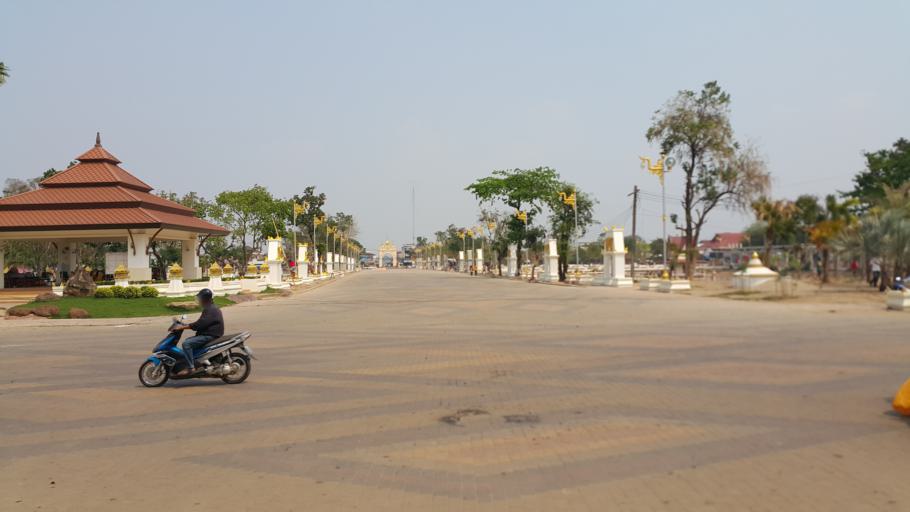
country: TH
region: Nakhon Phanom
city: That Phanom
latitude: 16.9426
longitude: 104.7246
